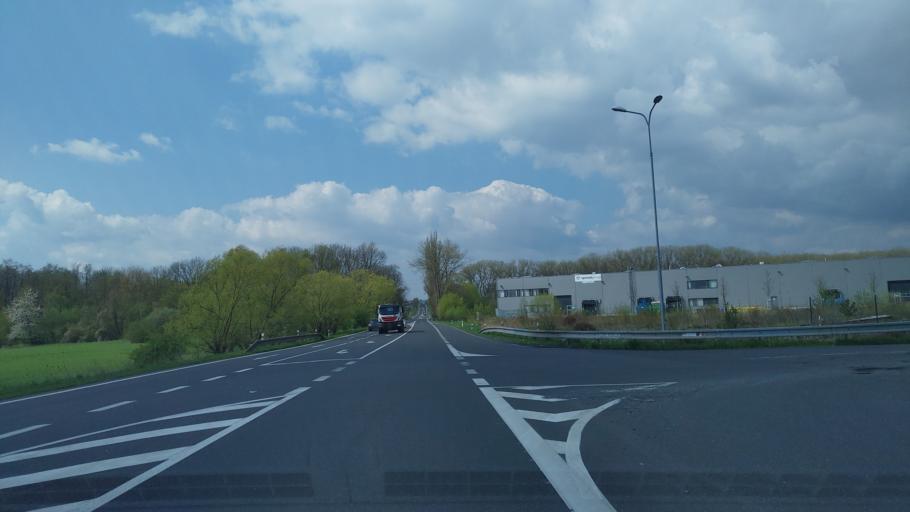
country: CZ
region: Ustecky
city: Krupka
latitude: 50.6676
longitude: 13.8848
